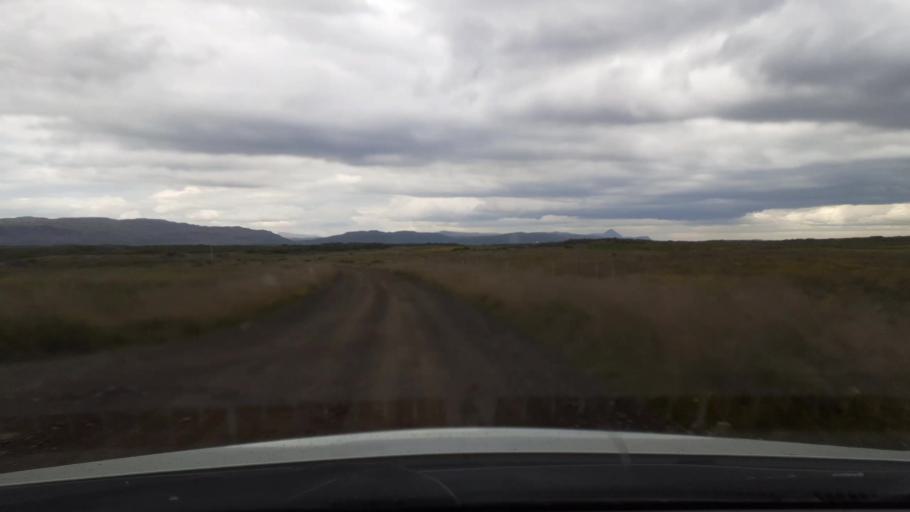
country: IS
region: West
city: Borgarnes
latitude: 64.6324
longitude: -21.9153
